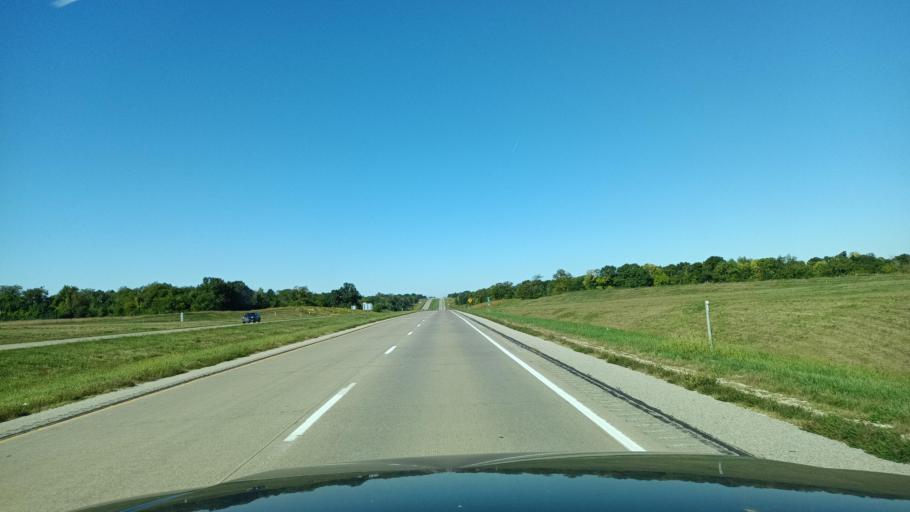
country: US
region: Iowa
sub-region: Lee County
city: Fort Madison
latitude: 40.6708
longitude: -91.2727
